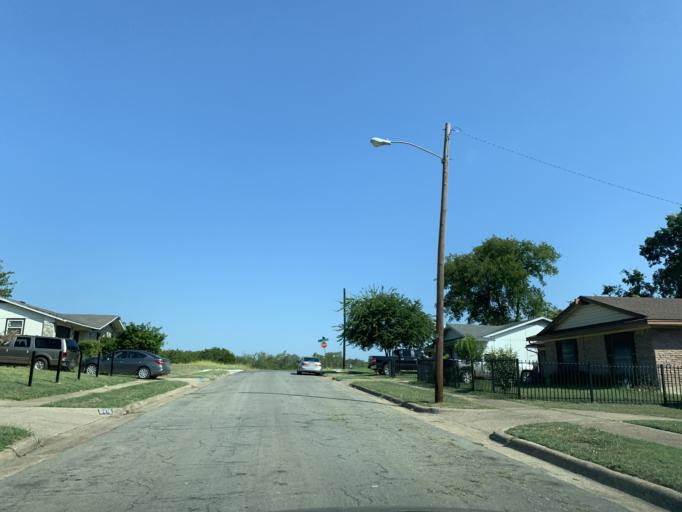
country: US
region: Texas
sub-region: Dallas County
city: Hutchins
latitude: 32.6680
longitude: -96.7539
